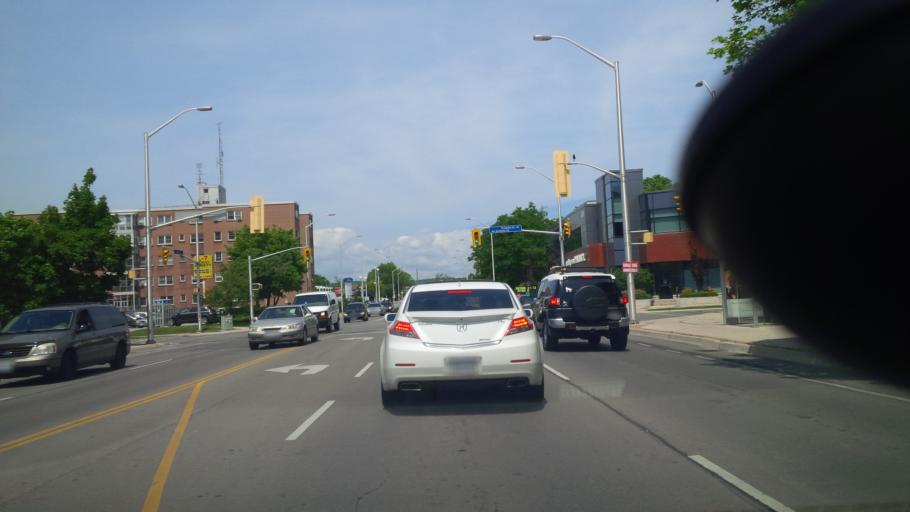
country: CA
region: Ontario
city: Burlington
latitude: 43.3338
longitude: -79.8096
